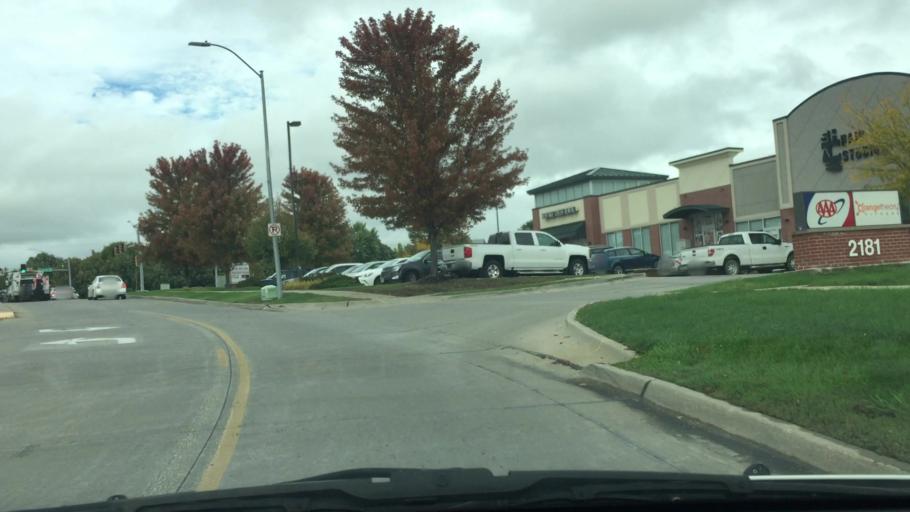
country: US
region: Iowa
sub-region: Polk County
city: Clive
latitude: 41.6138
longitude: -93.7715
